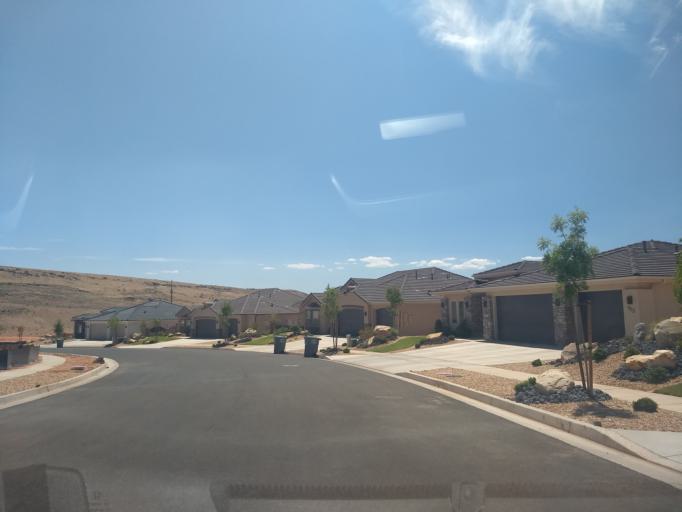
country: US
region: Utah
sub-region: Washington County
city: Washington
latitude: 37.1392
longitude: -113.4790
